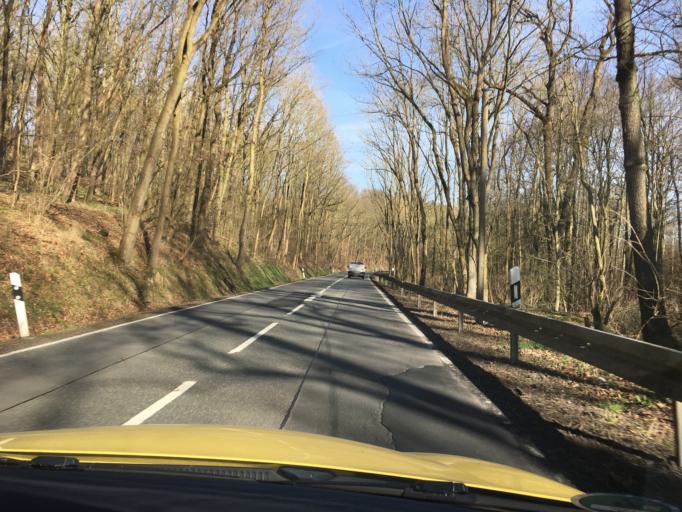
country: DE
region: Saxony-Anhalt
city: Bad Bibra
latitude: 51.2138
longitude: 11.5395
